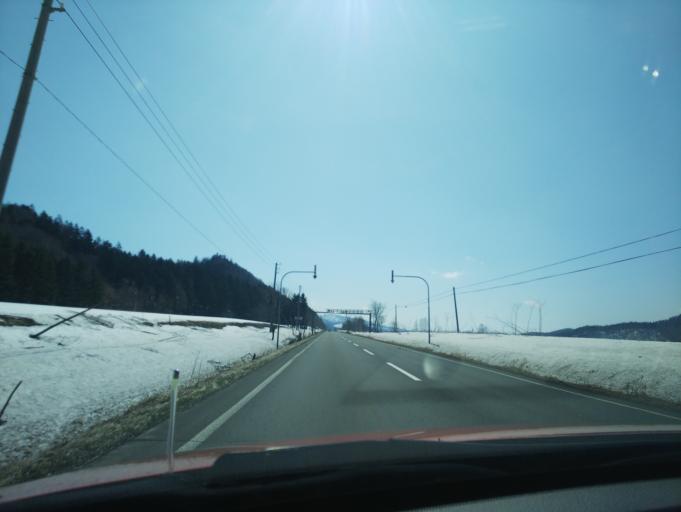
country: JP
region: Hokkaido
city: Nayoro
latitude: 44.6325
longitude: 142.2806
